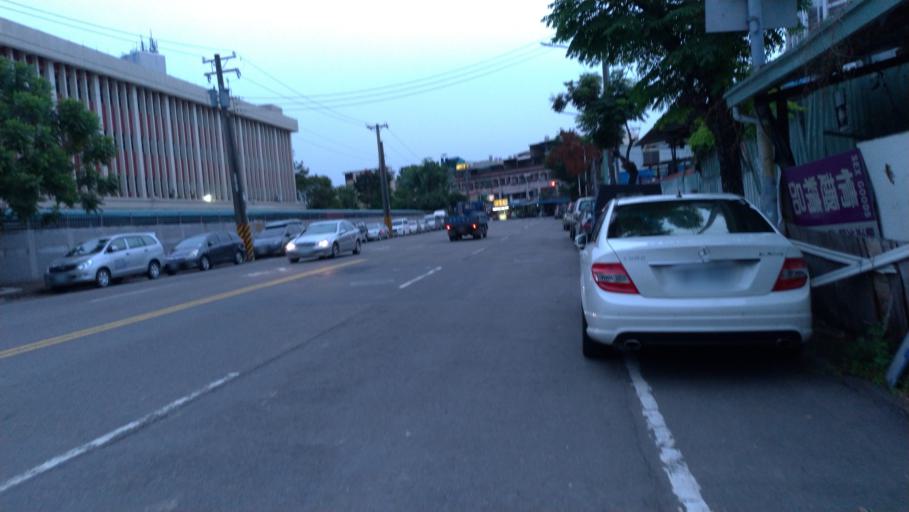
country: TW
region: Taiwan
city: Fengshan
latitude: 22.6549
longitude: 120.3623
